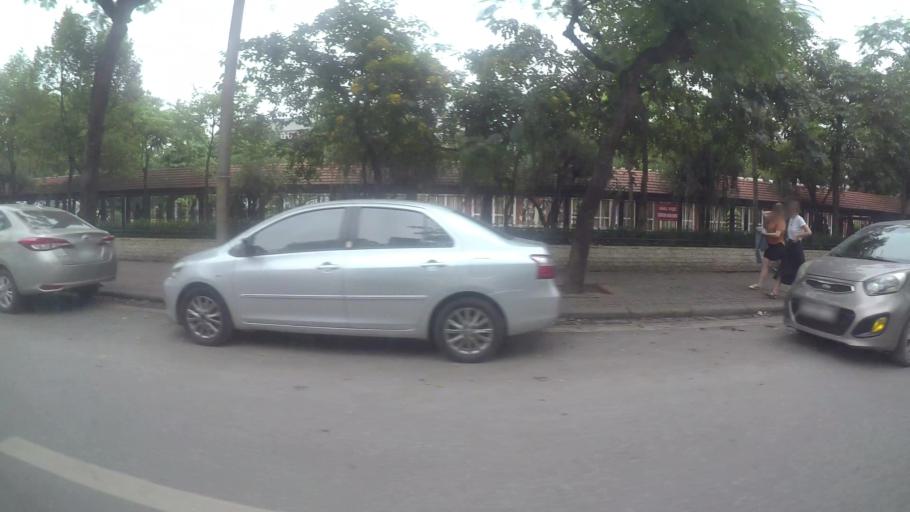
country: VN
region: Ha Noi
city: Hanoi
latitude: 21.0344
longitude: 105.8329
